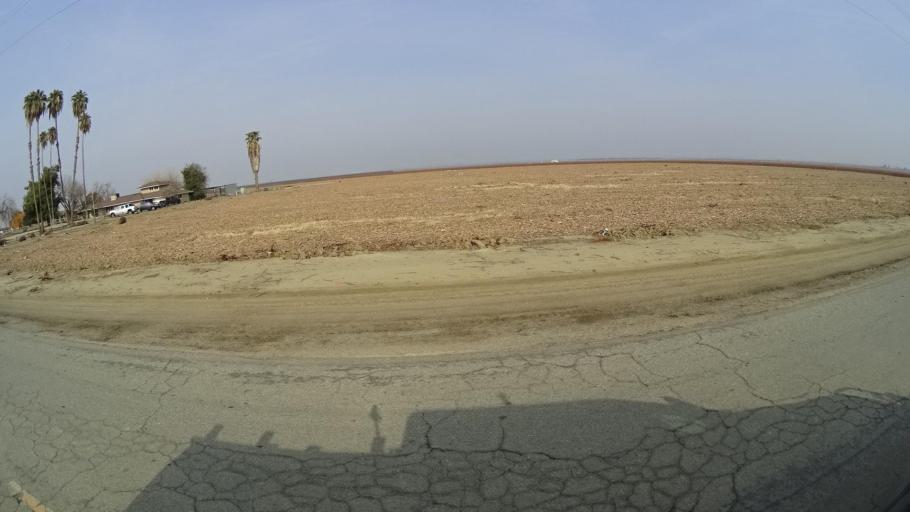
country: US
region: California
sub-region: Kern County
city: Greenfield
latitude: 35.0766
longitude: -119.0807
